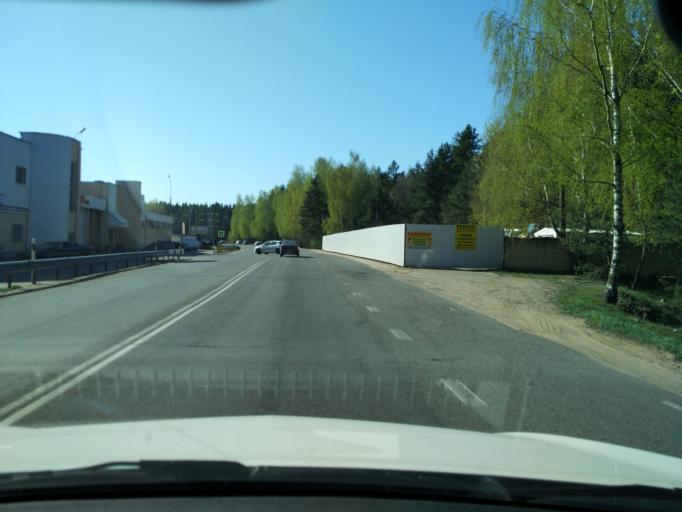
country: BY
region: Minsk
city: Lyeskawka
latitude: 53.9587
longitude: 27.7229
